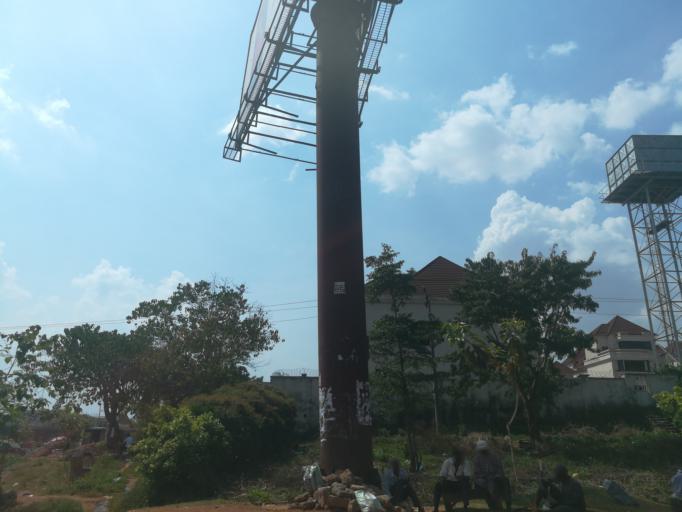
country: NG
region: Abuja Federal Capital Territory
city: Abuja
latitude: 9.0583
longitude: 7.4533
